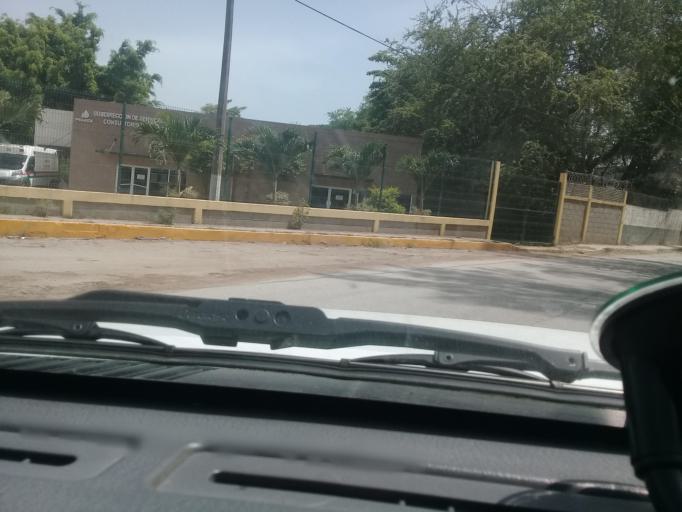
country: MX
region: Veracruz
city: Anahuac
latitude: 22.2287
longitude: -97.8315
